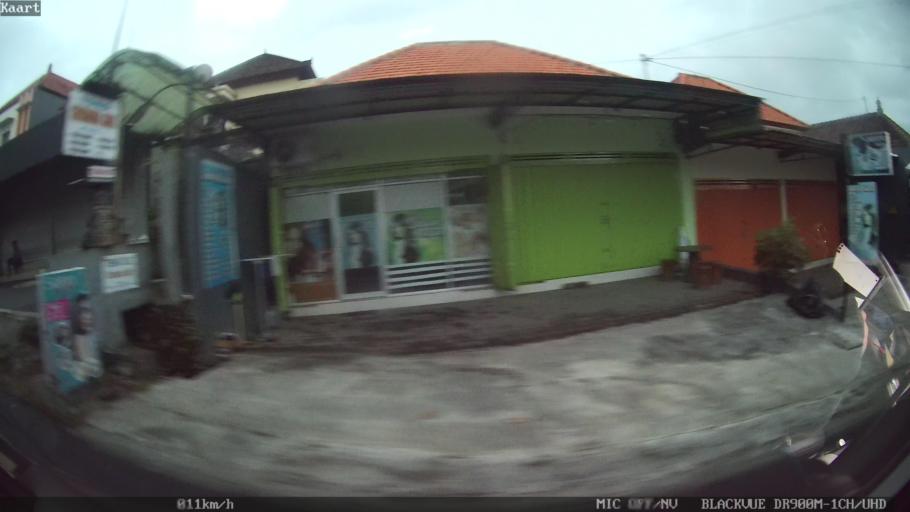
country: ID
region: Bali
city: Banjar Pasekan
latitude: -8.6150
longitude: 115.2795
